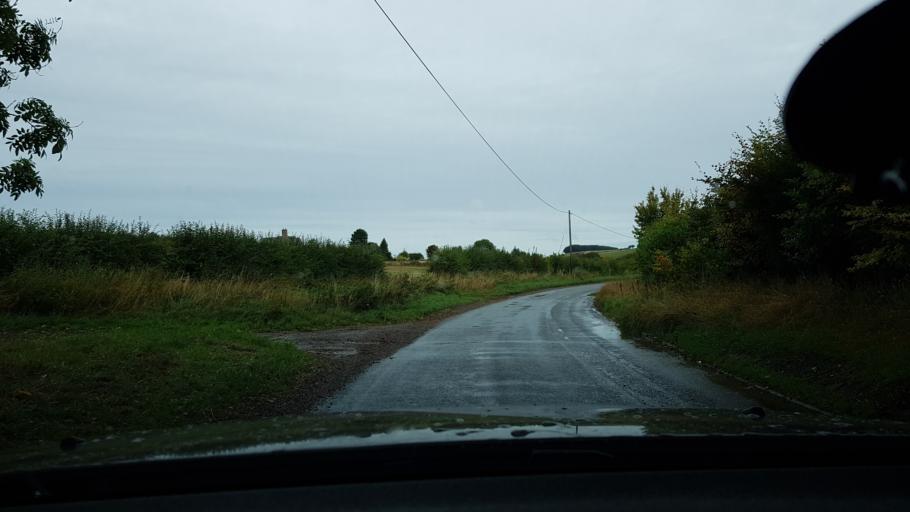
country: GB
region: England
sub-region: West Berkshire
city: Lambourn
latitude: 51.5383
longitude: -1.5297
